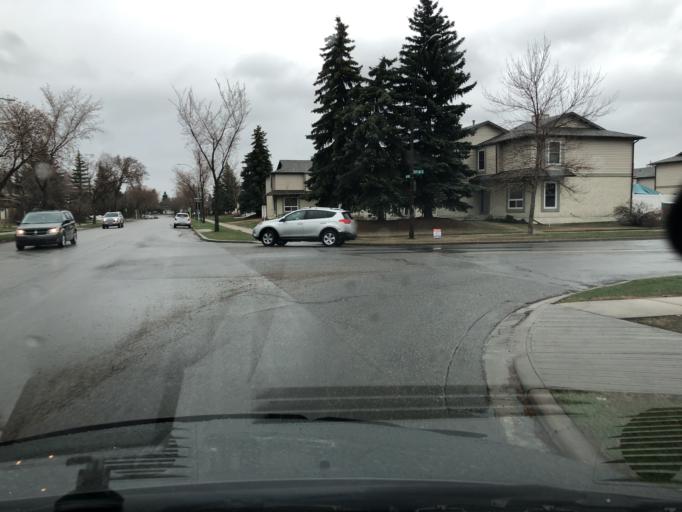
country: CA
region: Alberta
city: Calgary
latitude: 50.9284
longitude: -114.0265
